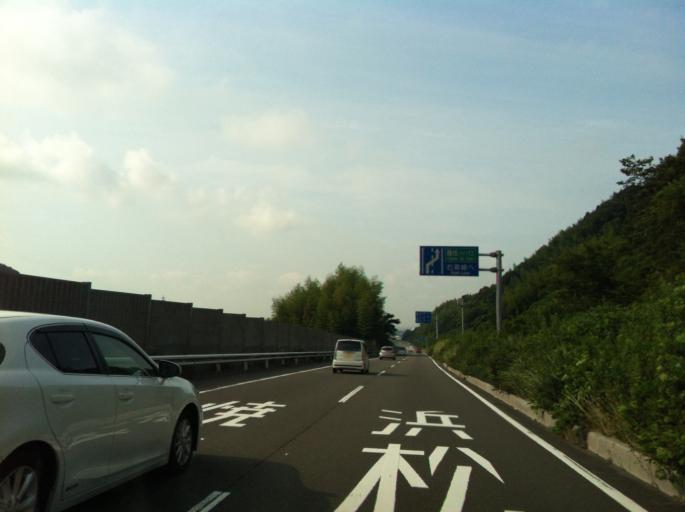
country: JP
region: Shizuoka
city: Fujieda
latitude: 34.9153
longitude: 138.2906
